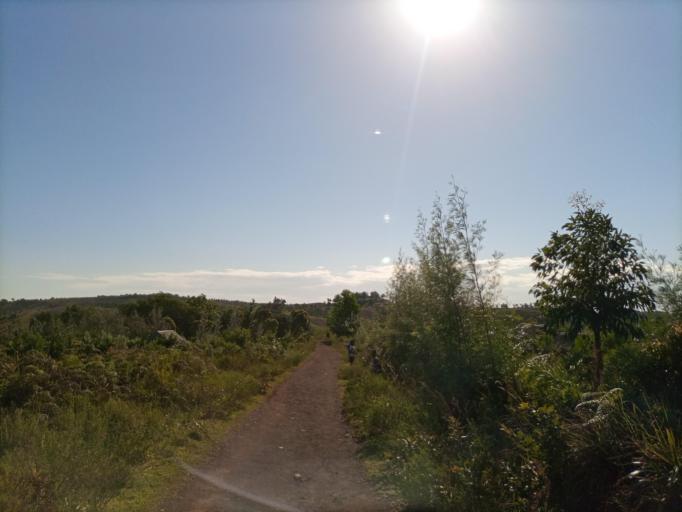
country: MG
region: Atsimo-Atsinanana
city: Vohipaho
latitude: -23.6054
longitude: 47.5182
